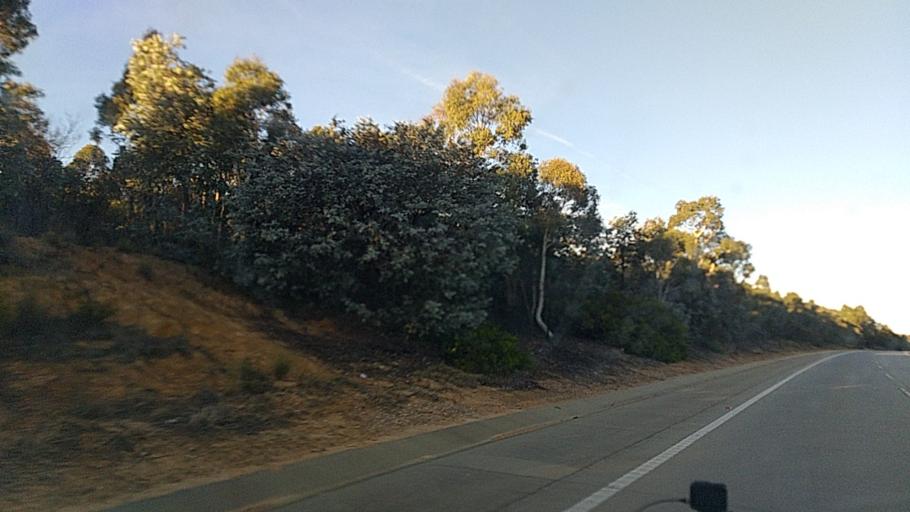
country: AU
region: New South Wales
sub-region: Yass Valley
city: Gundaroo
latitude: -35.1099
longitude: 149.3685
